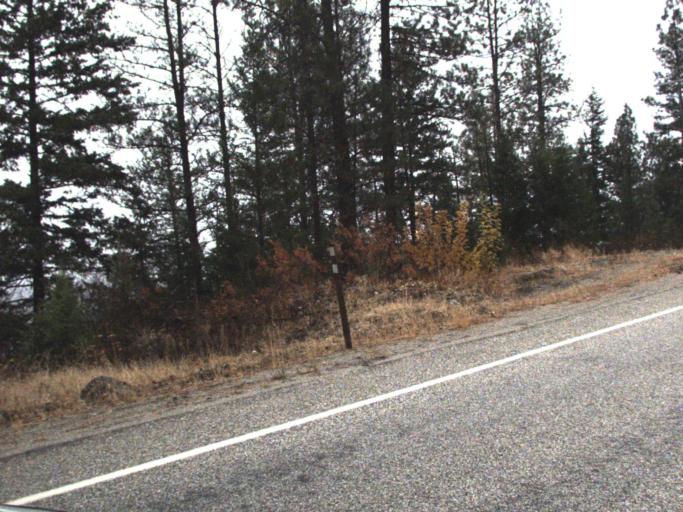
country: US
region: Washington
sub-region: Stevens County
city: Kettle Falls
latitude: 48.7452
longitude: -118.1332
